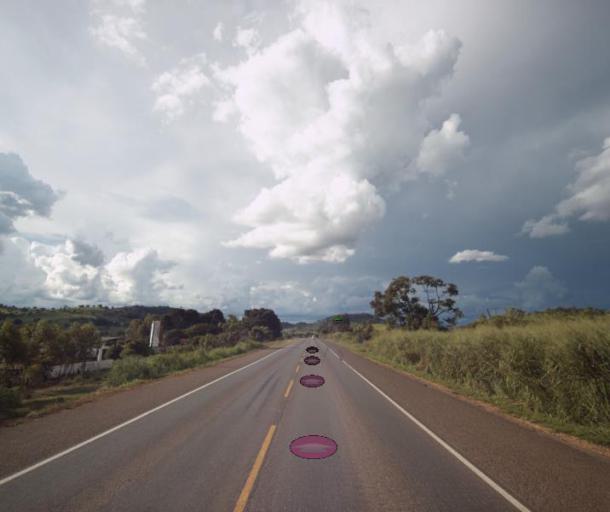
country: BR
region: Goias
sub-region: Rialma
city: Rialma
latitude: -15.2996
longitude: -49.5699
